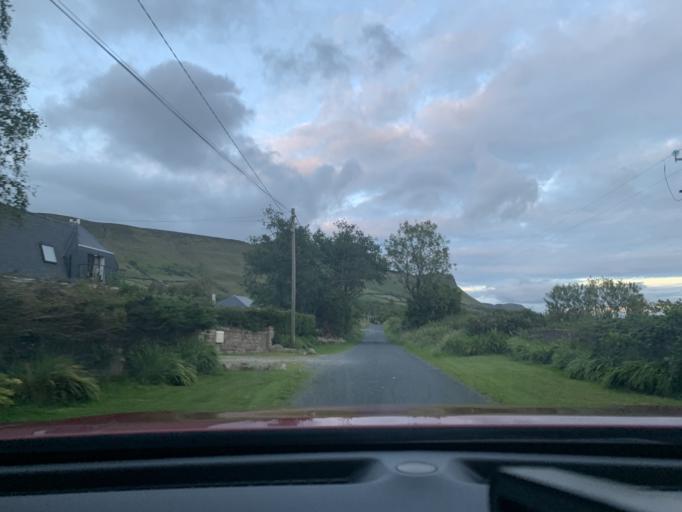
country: IE
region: Connaught
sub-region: Sligo
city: Sligo
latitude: 54.3546
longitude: -8.4935
